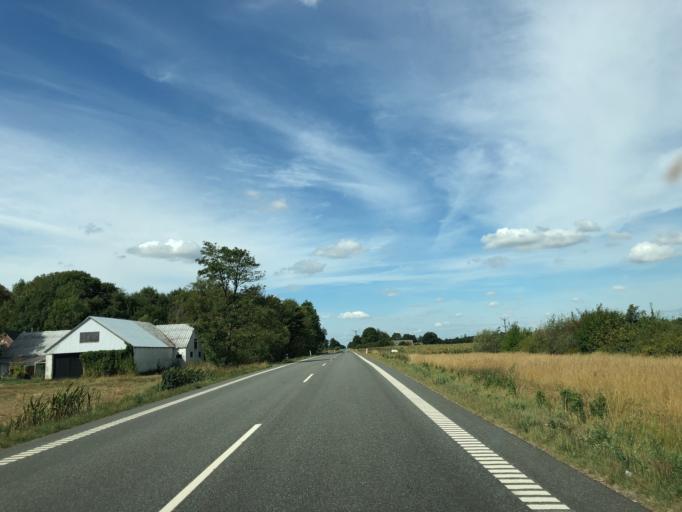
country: DK
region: Central Jutland
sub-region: Ikast-Brande Kommune
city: Bording Kirkeby
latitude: 56.1373
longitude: 9.3346
